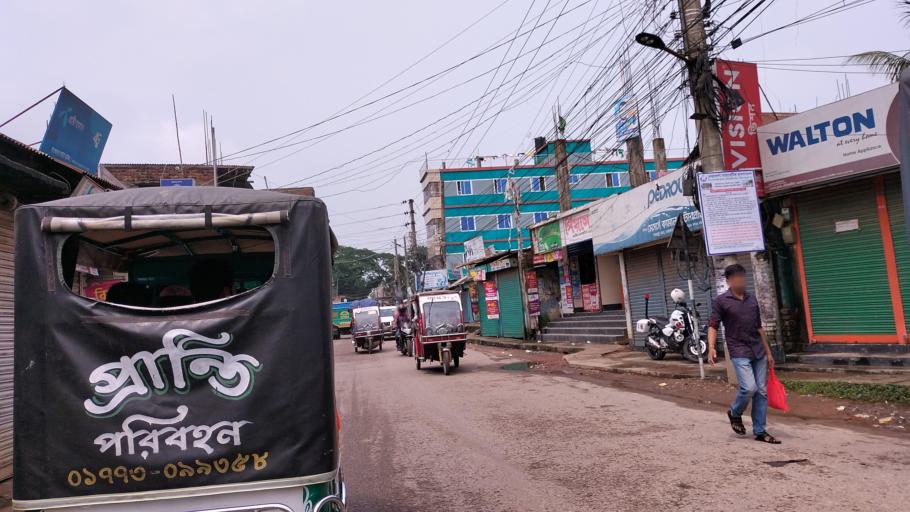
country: BD
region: Dhaka
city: Netrakona
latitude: 24.8858
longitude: 90.7352
